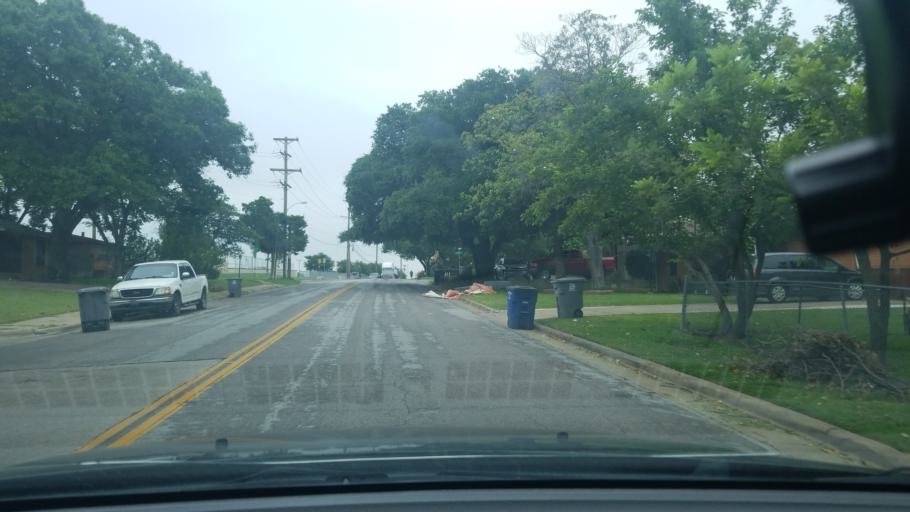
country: US
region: Texas
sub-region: Dallas County
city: Balch Springs
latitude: 32.7582
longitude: -96.6934
